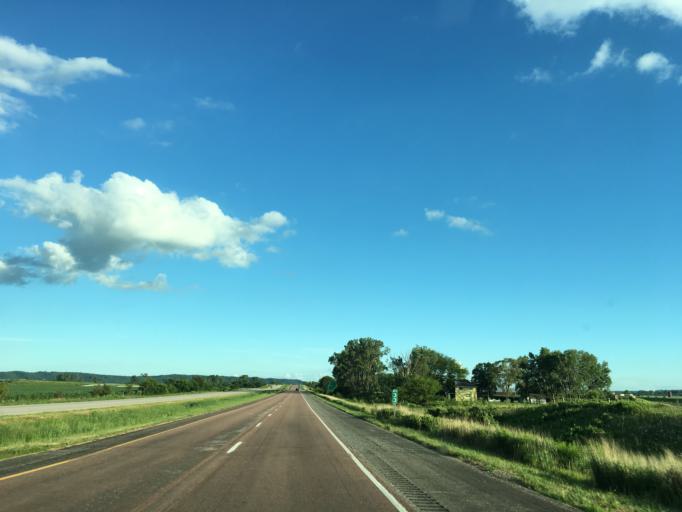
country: US
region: Nebraska
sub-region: Cass County
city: Plattsmouth
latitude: 41.0102
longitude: -95.8095
